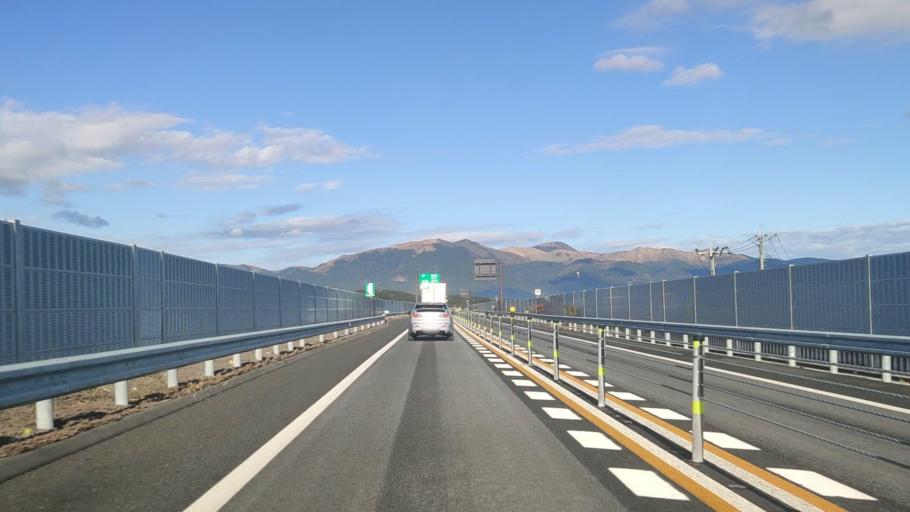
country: JP
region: Fukuoka
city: Yukuhashi
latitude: 33.7090
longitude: 130.9557
